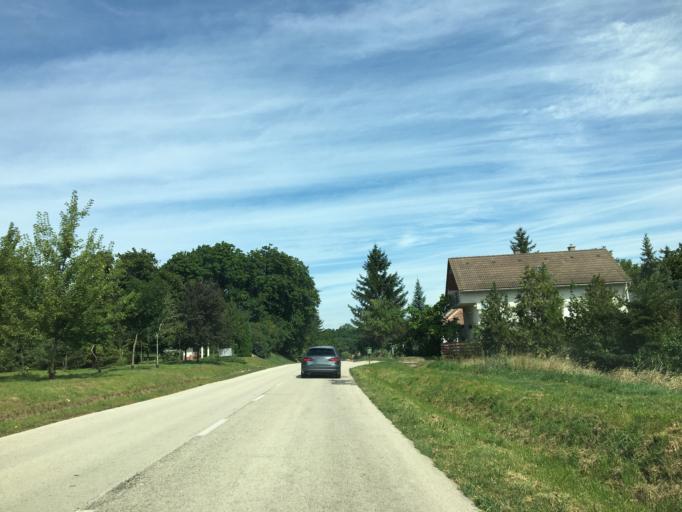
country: HU
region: Komarom-Esztergom
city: Bajna
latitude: 47.6437
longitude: 18.6053
